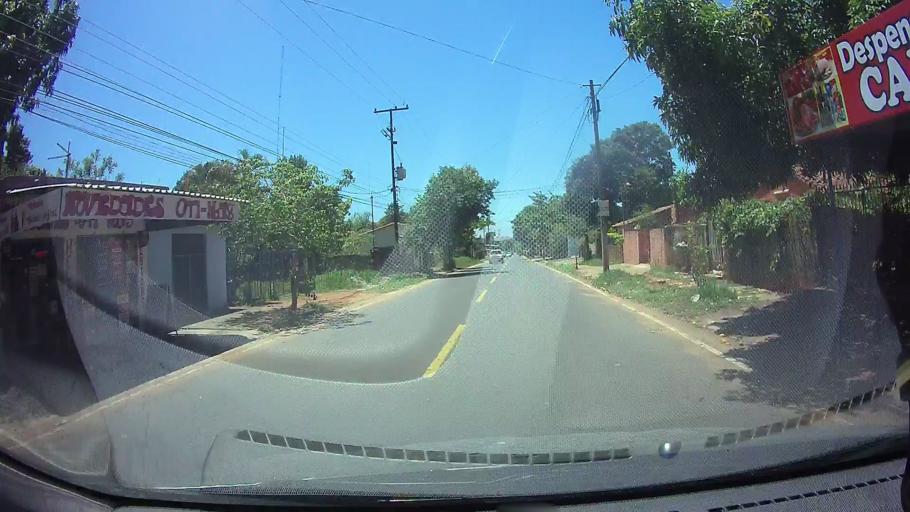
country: PY
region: Central
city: San Lorenzo
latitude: -25.3184
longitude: -57.4921
